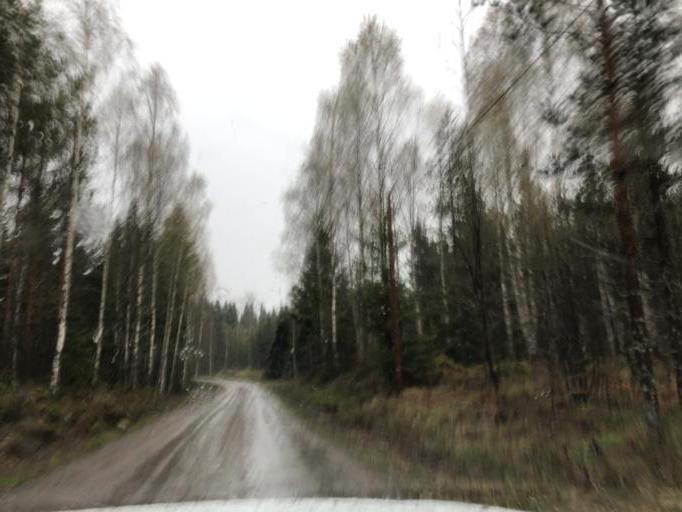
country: SE
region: Uppsala
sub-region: Heby Kommun
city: Tarnsjo
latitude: 60.2051
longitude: 16.8908
